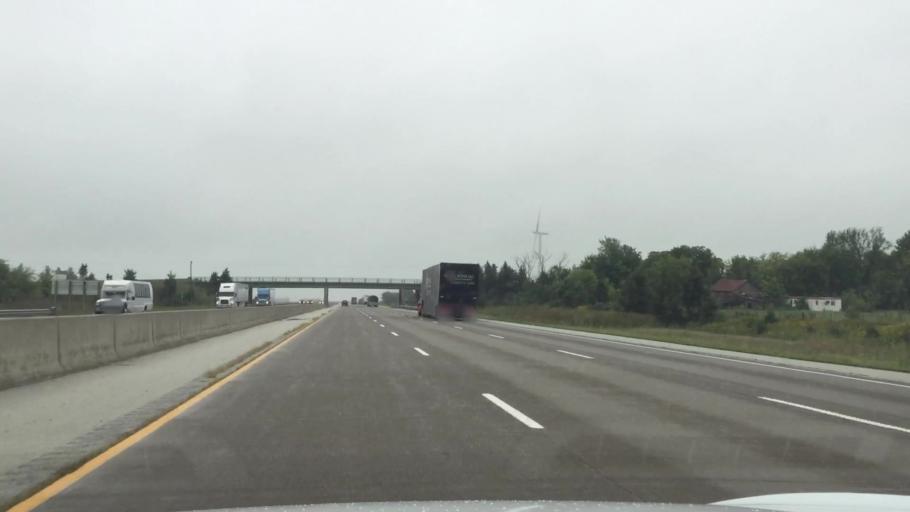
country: US
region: Michigan
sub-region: Wayne County
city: Grosse Pointe Farms
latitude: 42.2361
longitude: -82.6898
